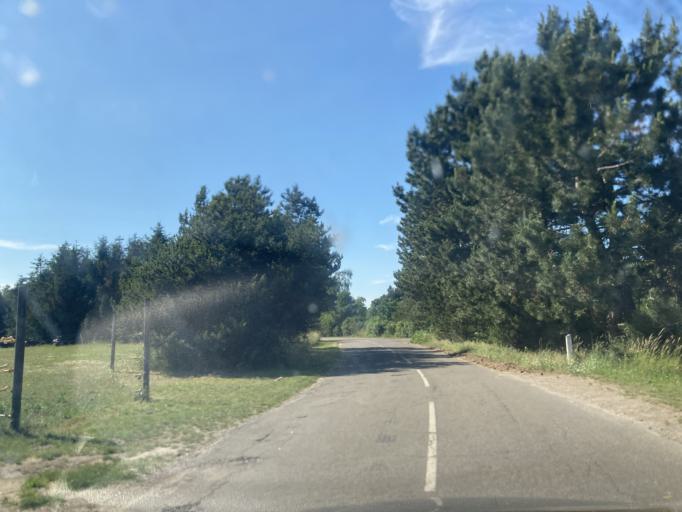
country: DK
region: Capital Region
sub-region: Halsnaes Kommune
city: Liseleje
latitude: 56.0041
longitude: 11.9773
